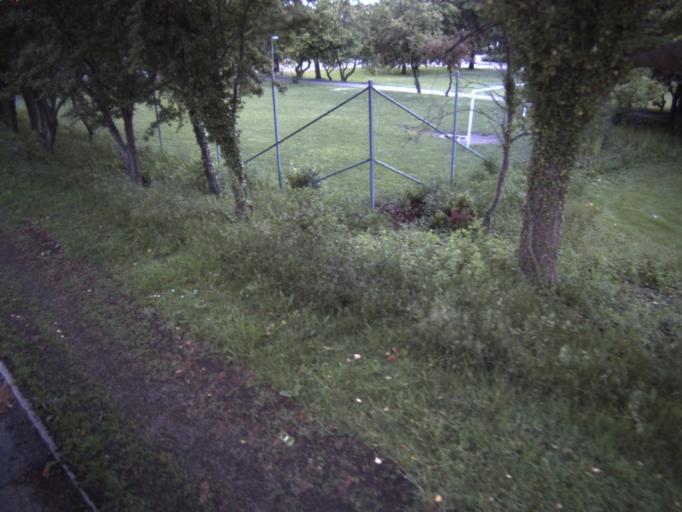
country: SE
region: Skane
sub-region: Helsingborg
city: Helsingborg
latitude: 56.0395
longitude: 12.7189
